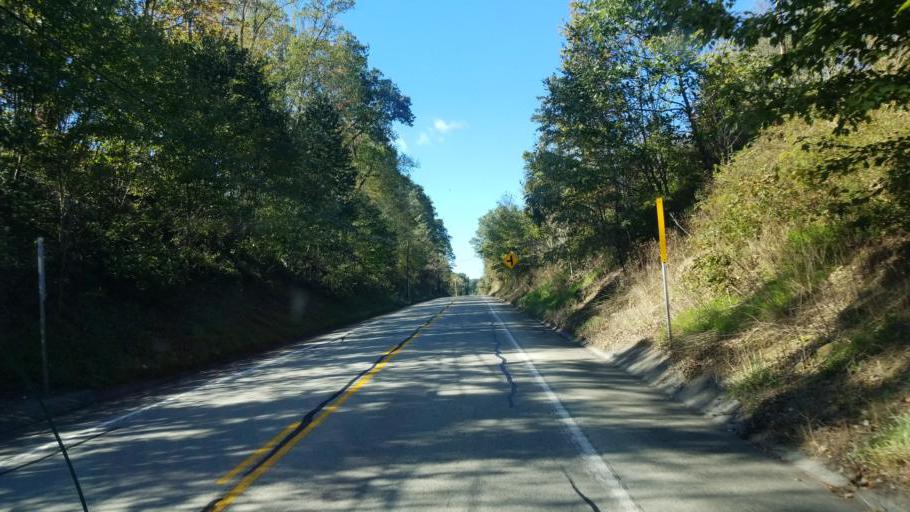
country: US
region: Pennsylvania
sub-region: Somerset County
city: Boswell
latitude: 40.1679
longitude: -79.0991
